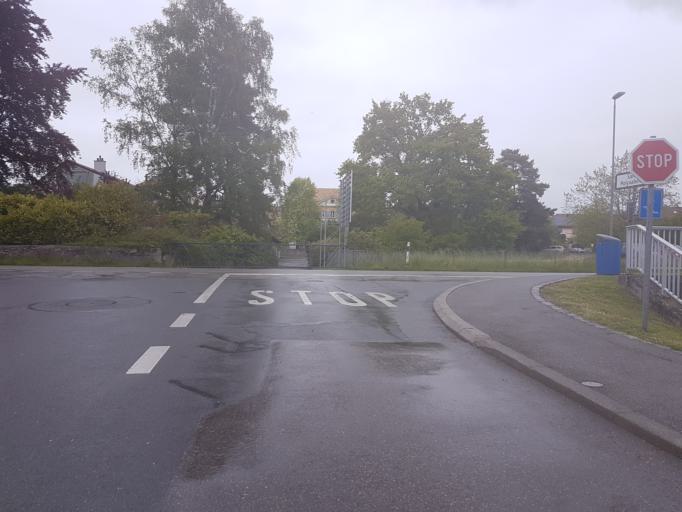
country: CH
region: Vaud
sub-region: Morges District
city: Preverenges
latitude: 46.5167
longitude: 6.5284
